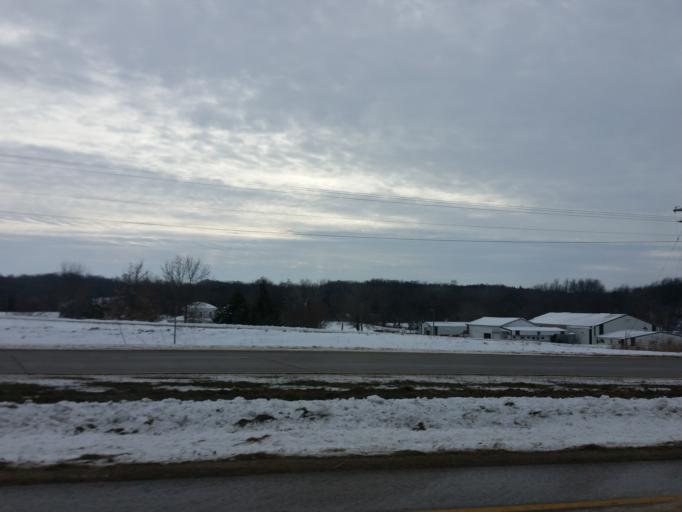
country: US
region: Iowa
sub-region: Dubuque County
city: Dyersville
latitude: 42.4695
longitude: -91.0963
